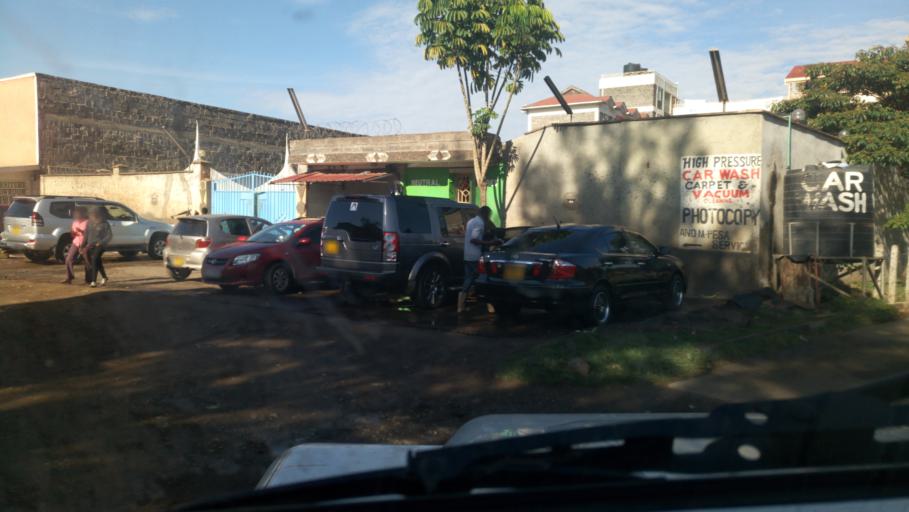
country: KE
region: Nakuru
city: Nakuru
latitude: -0.2975
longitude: 36.0722
